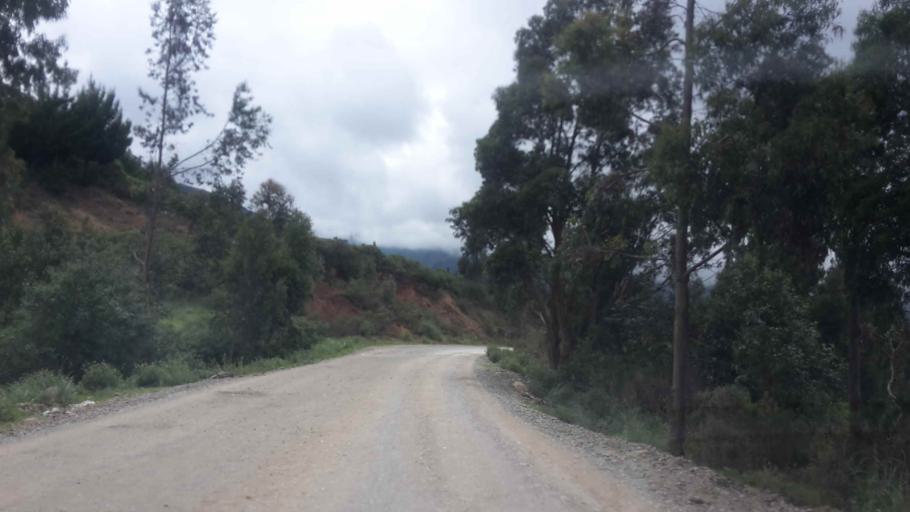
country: BO
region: Cochabamba
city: Totora
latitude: -17.5690
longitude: -65.3234
